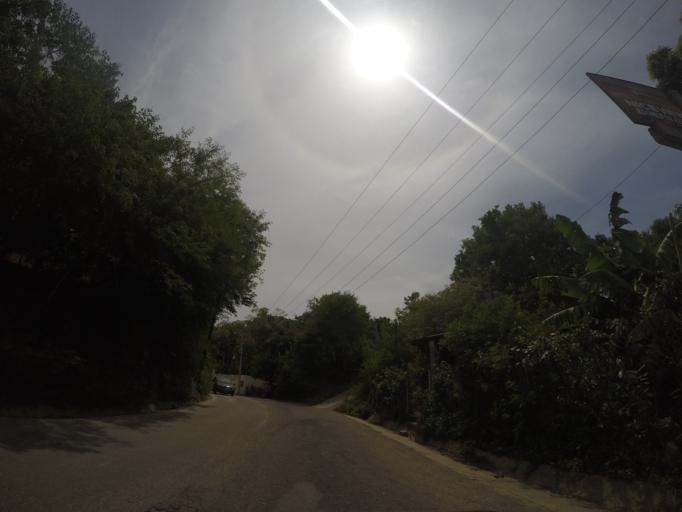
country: MX
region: Oaxaca
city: San Pedro Pochutla
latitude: 15.6683
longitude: -96.4967
